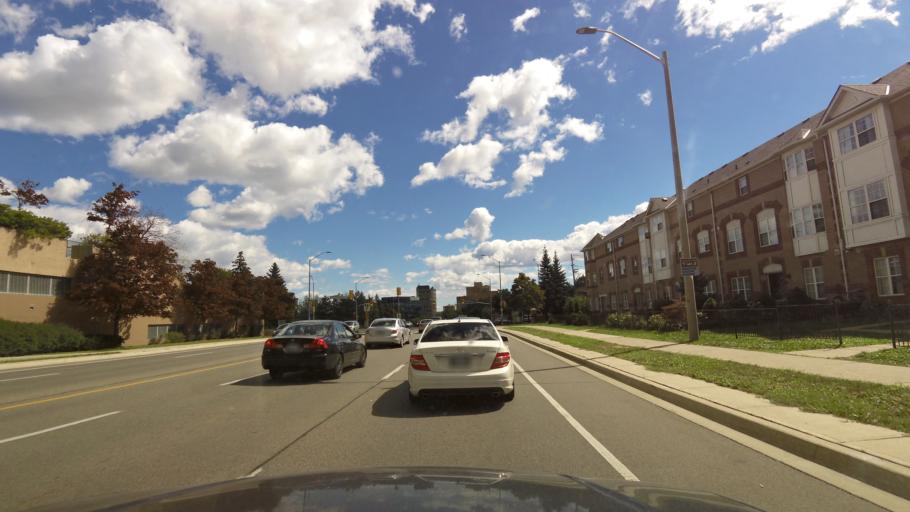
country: CA
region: Ontario
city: Mississauga
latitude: 43.5796
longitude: -79.6251
